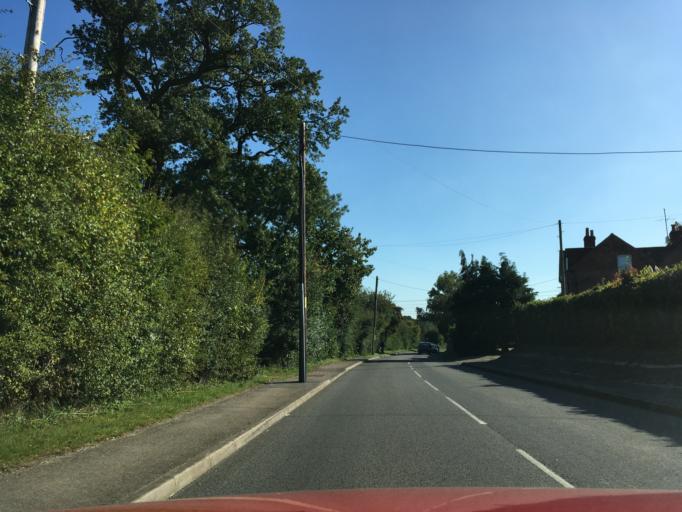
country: GB
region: England
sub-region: West Berkshire
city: Cold Ash
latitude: 51.4177
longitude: -1.2627
